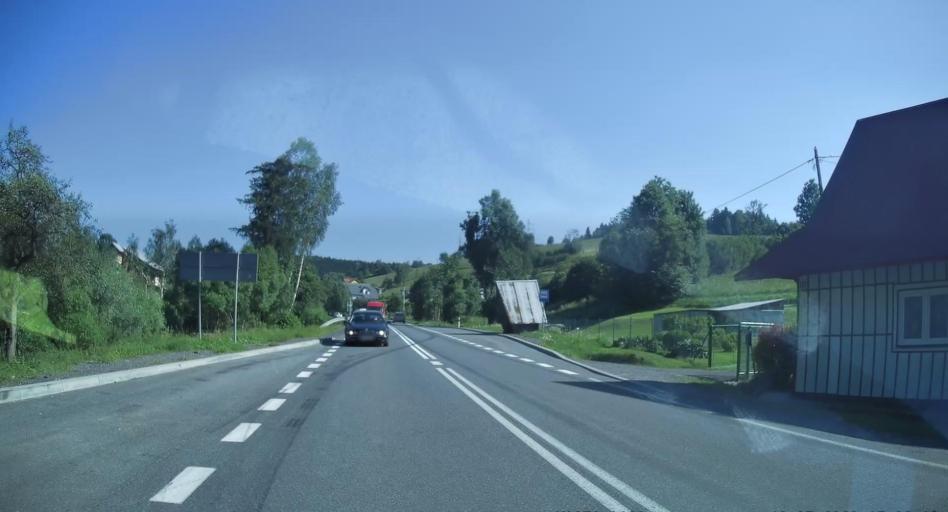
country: PL
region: Lesser Poland Voivodeship
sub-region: Powiat nowosadecki
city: Labowa
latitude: 49.4851
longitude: 20.9151
